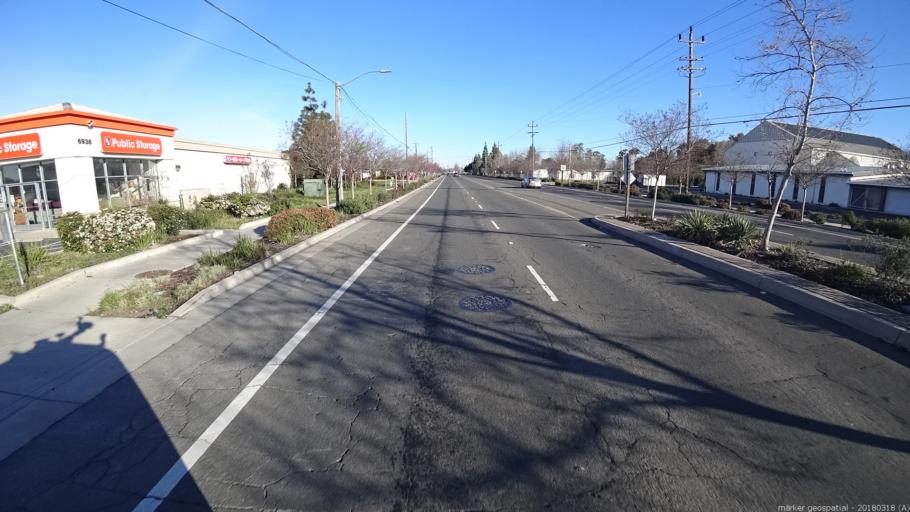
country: US
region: California
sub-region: Sacramento County
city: Parkway
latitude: 38.5011
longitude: -121.4621
